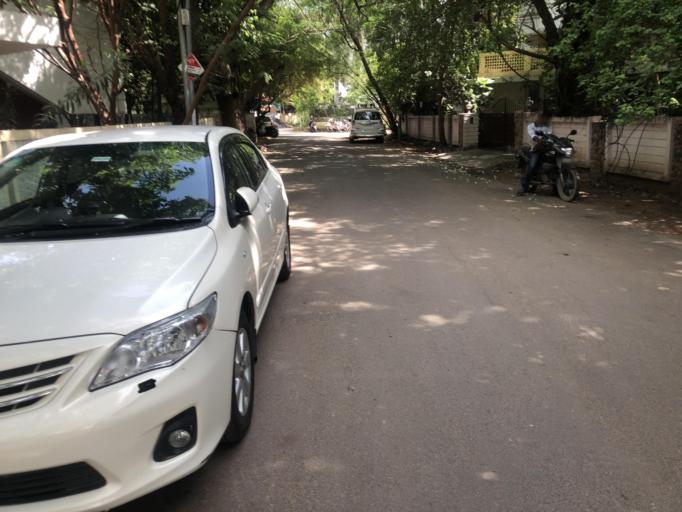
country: IN
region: Tamil Nadu
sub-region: Chennai
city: Gandhi Nagar
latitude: 13.0377
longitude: 80.2655
